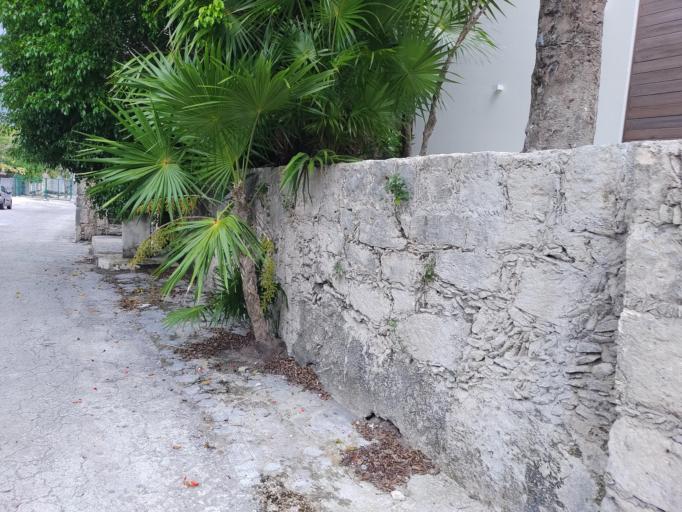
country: MX
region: Quintana Roo
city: San Miguel de Cozumel
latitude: 20.5288
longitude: -86.9401
